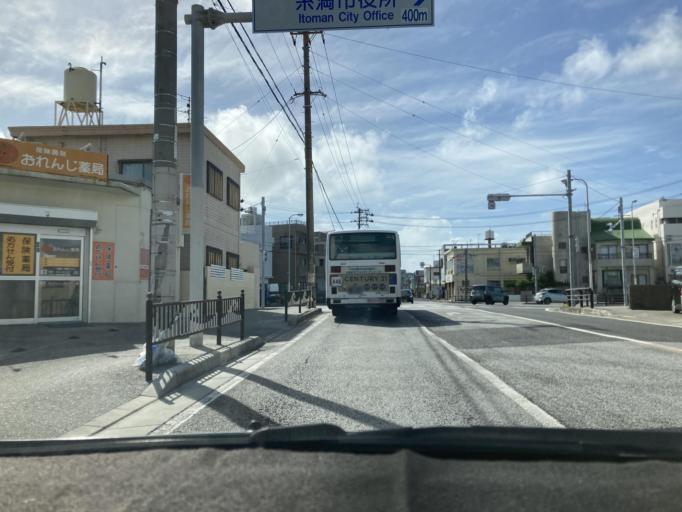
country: JP
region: Okinawa
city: Itoman
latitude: 26.1262
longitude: 127.6694
